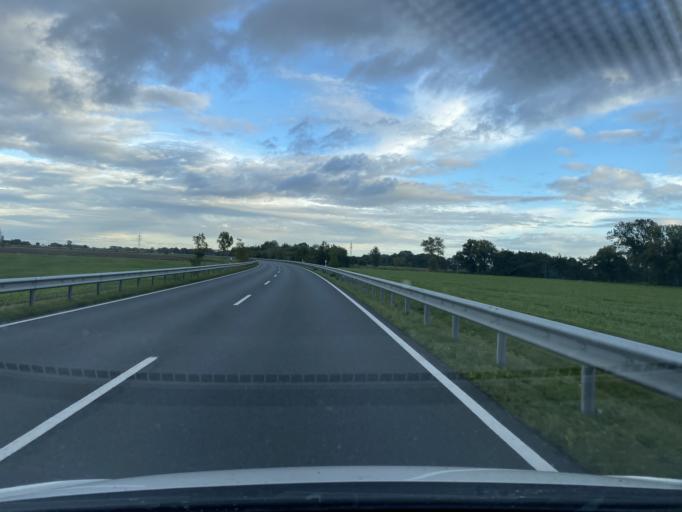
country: DE
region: Lower Saxony
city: Otterndorf
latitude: 53.7979
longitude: 8.8730
